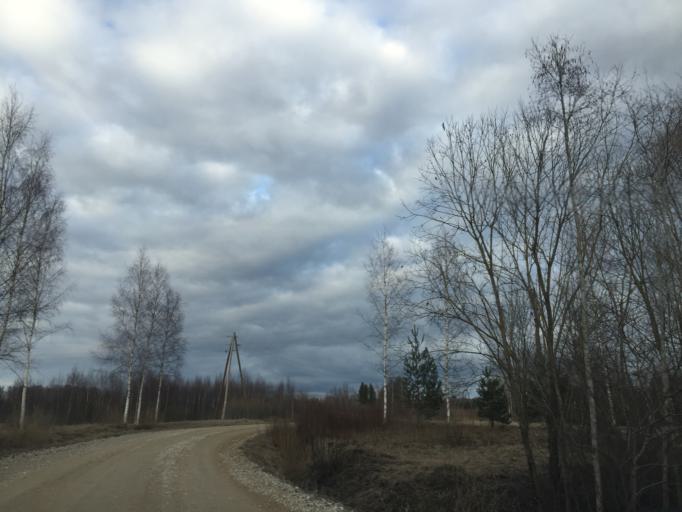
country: LV
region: Jaunjelgava
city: Jaunjelgava
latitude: 56.5967
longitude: 25.0534
